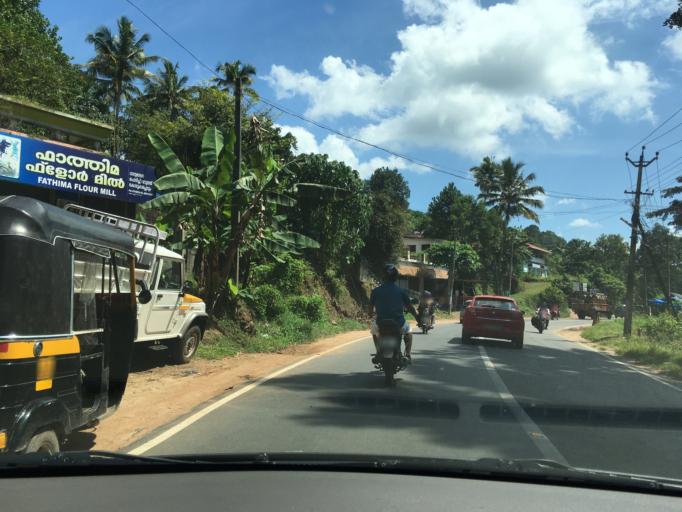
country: IN
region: Kerala
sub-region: Thiruvananthapuram
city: Nedumangad
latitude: 8.5873
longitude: 76.9955
